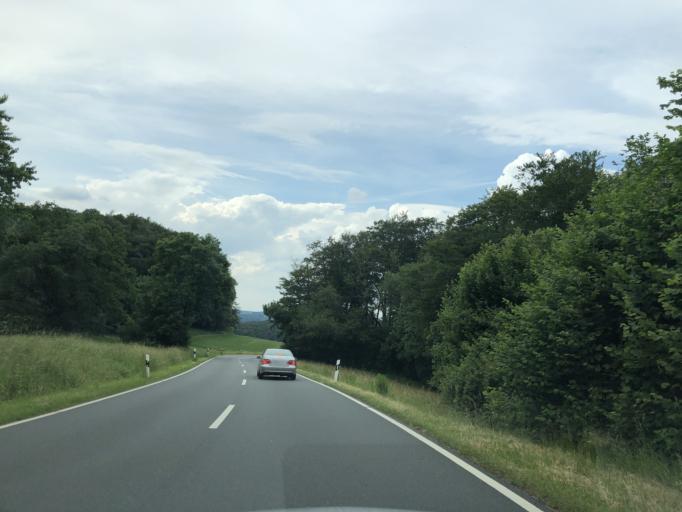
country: DE
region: Hesse
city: Lutzelbach
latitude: 49.7377
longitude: 8.7664
